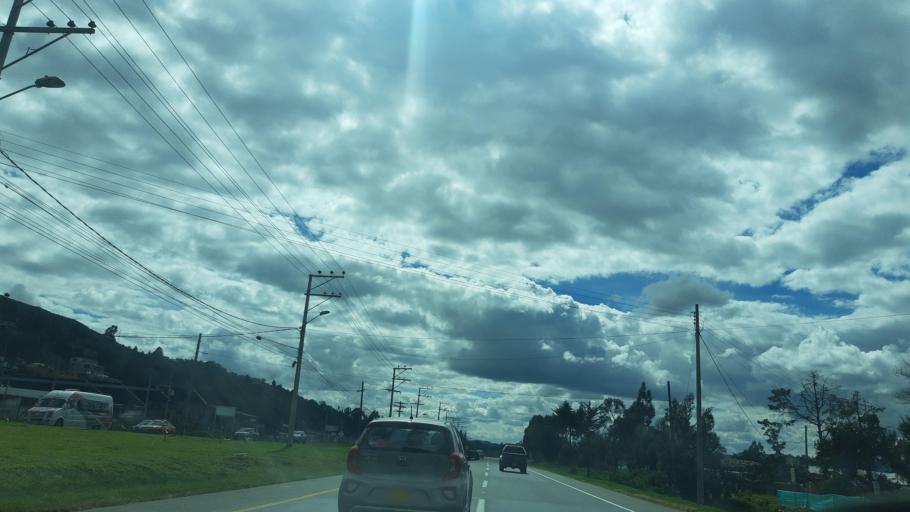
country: CO
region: Cundinamarca
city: Gachancipa
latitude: 4.9816
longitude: -73.8853
